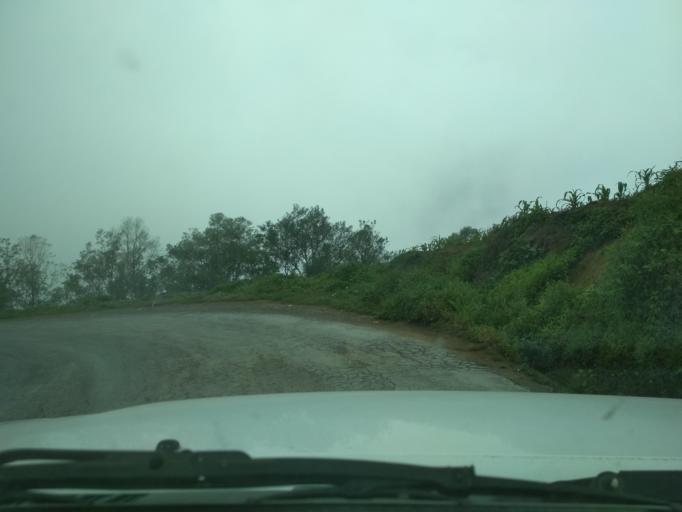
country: MX
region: Veracruz
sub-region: La Perla
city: Metlac Hernandez (Metlac Primero)
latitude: 18.9630
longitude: -97.1655
